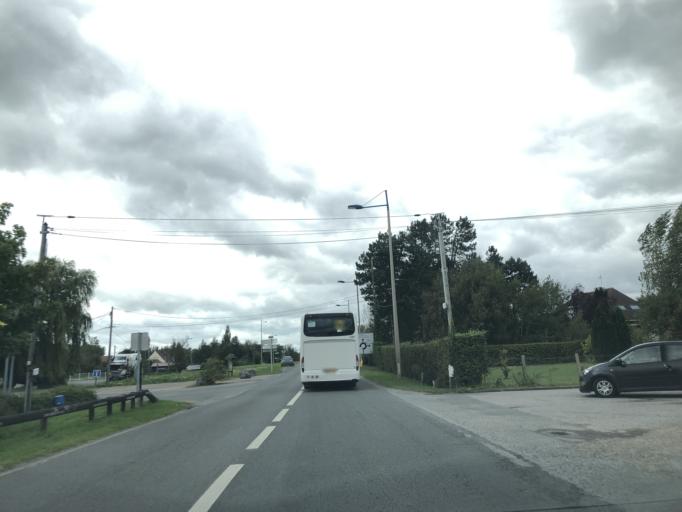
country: FR
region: Nord-Pas-de-Calais
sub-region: Departement du Pas-de-Calais
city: Saint-Josse
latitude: 50.4616
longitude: 1.6498
